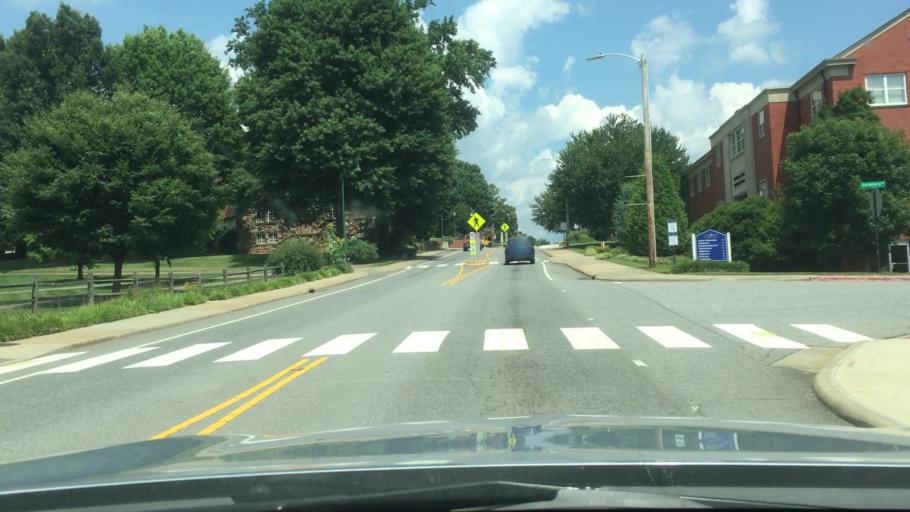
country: US
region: North Carolina
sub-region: Madison County
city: Mars Hill
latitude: 35.8264
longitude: -82.5522
